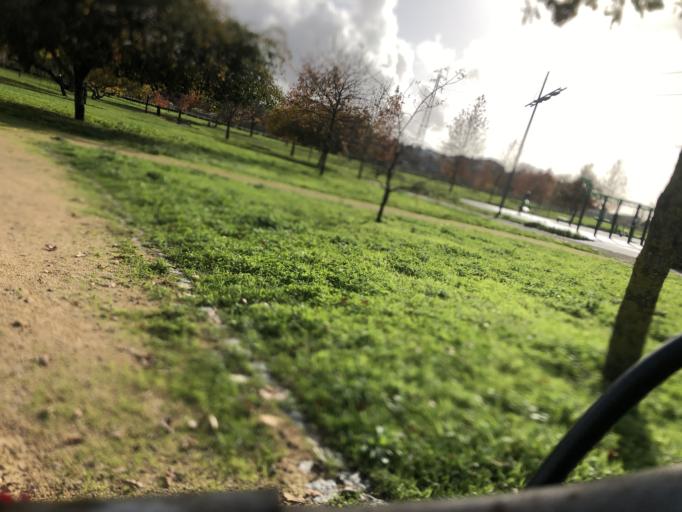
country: PT
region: Aveiro
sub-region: Estarreja
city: Estarreja
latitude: 40.7532
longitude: -8.5653
